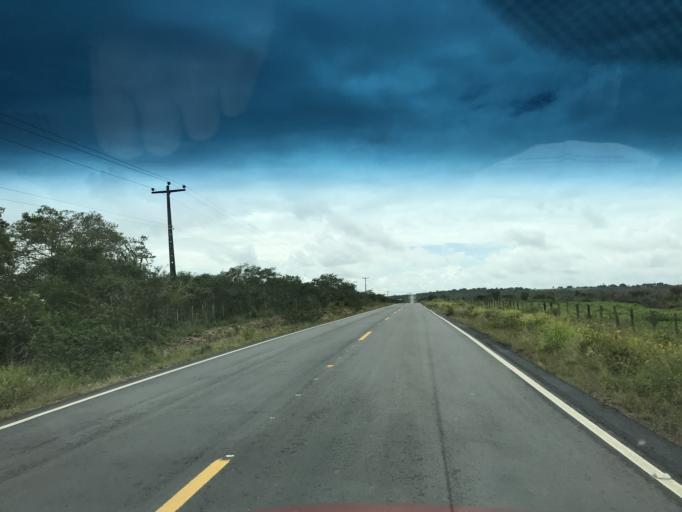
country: BR
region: Bahia
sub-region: Castro Alves
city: Castro Alves
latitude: -12.6760
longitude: -39.2969
